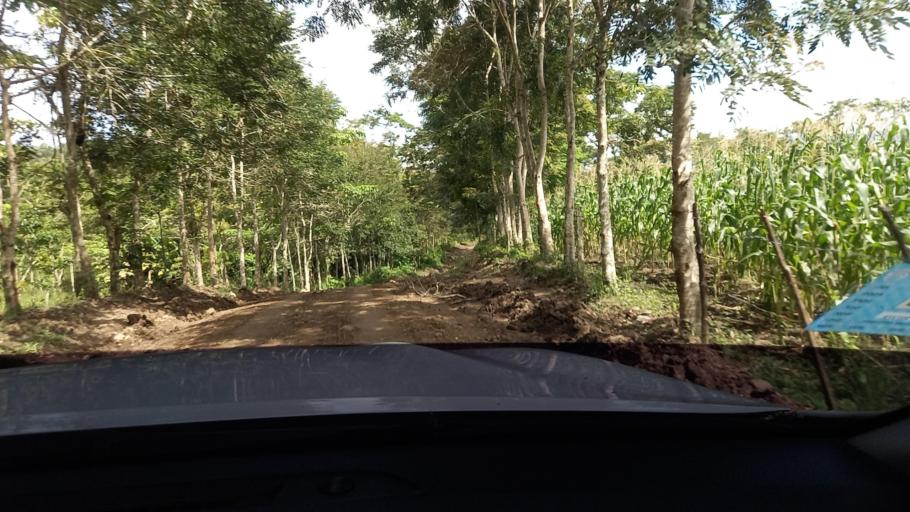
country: NI
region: Jinotega
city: San Jose de Bocay
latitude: 13.3831
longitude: -85.6878
